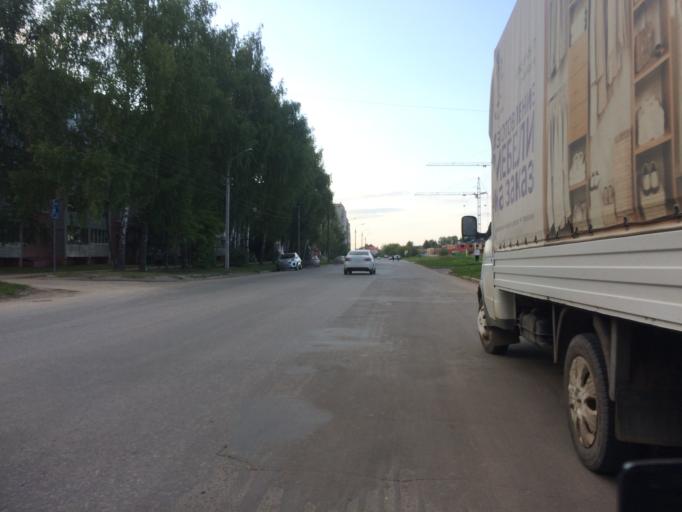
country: RU
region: Mariy-El
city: Medvedevo
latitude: 56.6425
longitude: 47.8449
